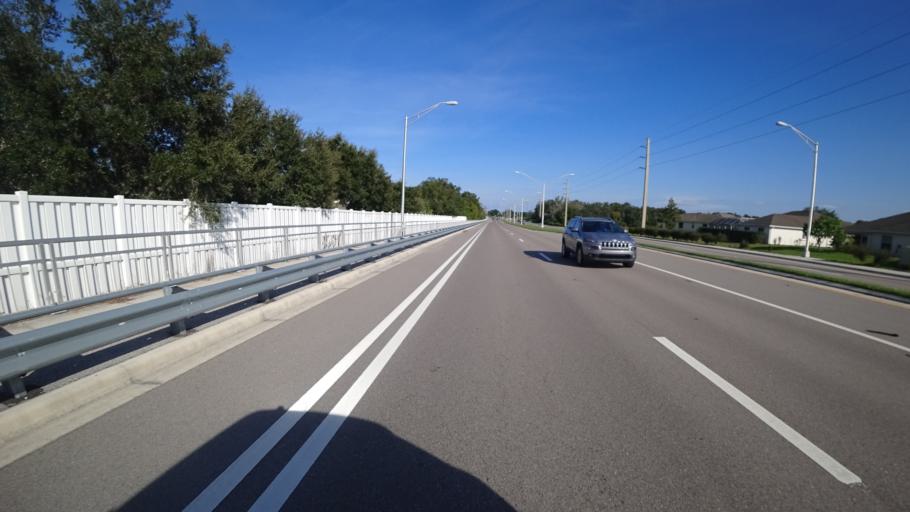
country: US
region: Florida
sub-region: Manatee County
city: Samoset
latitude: 27.4615
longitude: -82.5203
